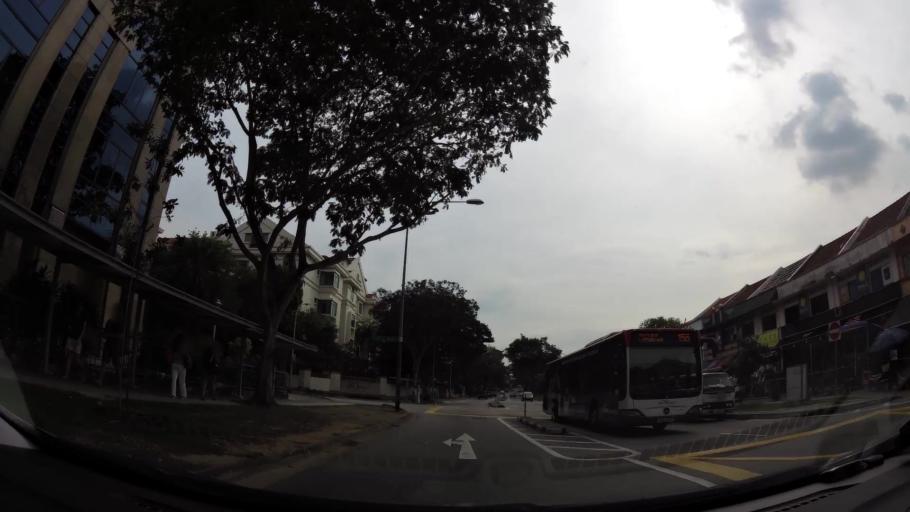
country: SG
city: Singapore
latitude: 1.3309
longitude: 103.7953
